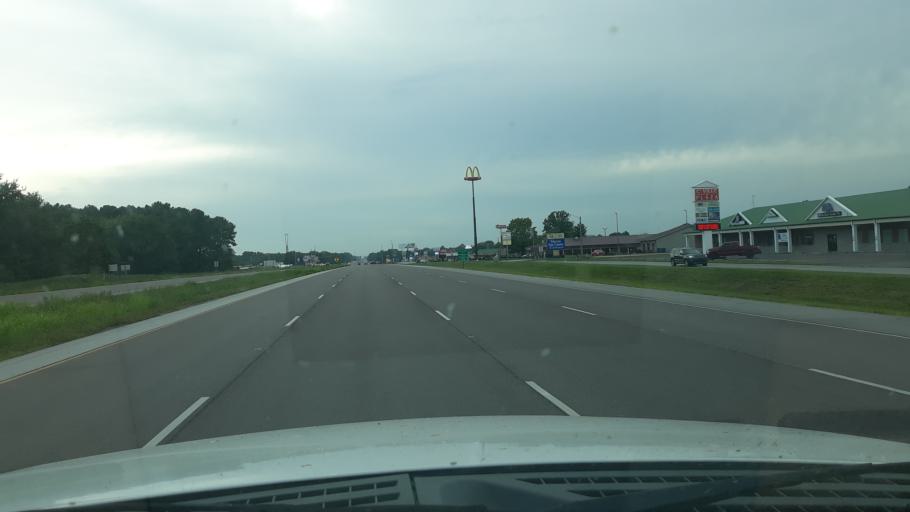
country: US
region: Illinois
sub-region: Williamson County
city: Crainville
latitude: 37.7452
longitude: -89.0708
